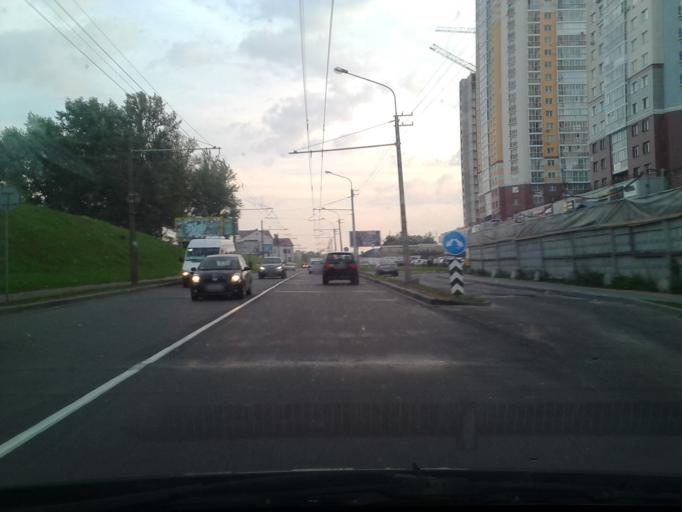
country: BY
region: Minsk
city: Minsk
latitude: 53.9378
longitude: 27.5834
